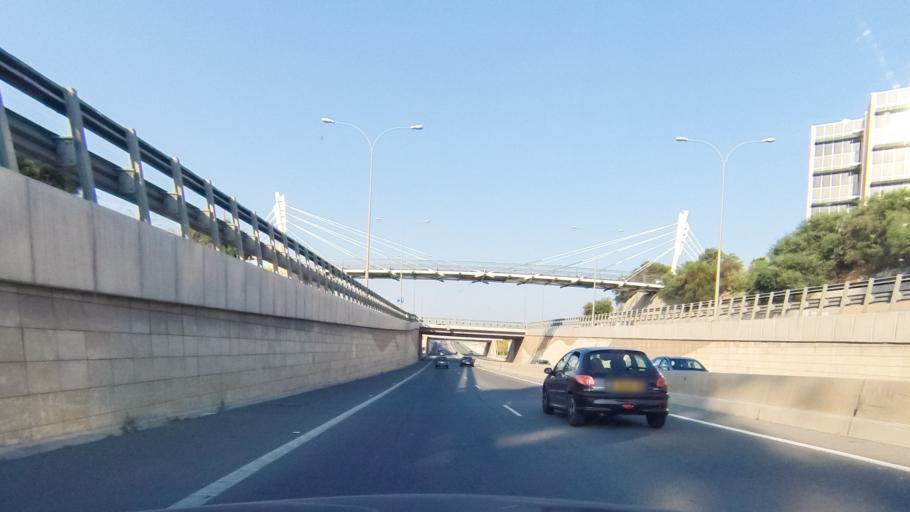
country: CY
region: Limassol
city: Limassol
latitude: 34.7068
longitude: 33.0585
